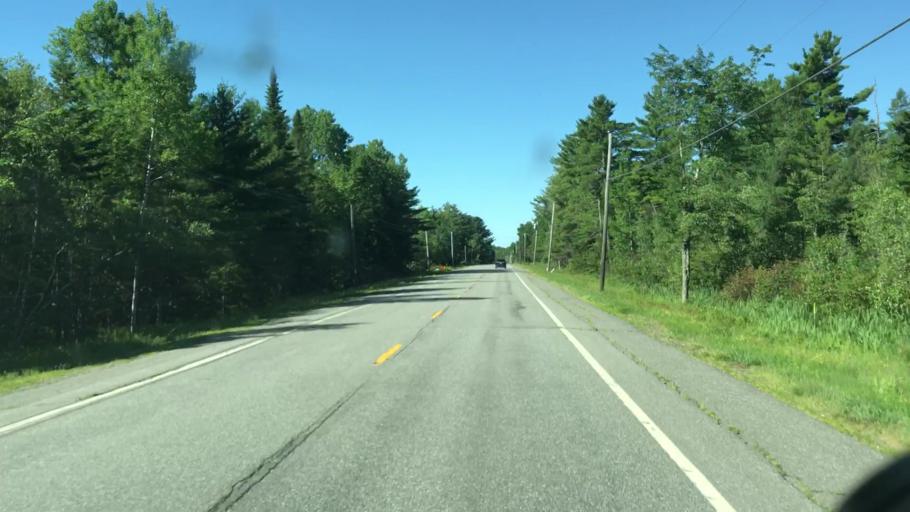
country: US
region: Maine
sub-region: Penobscot County
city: Howland
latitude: 45.2814
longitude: -68.6297
